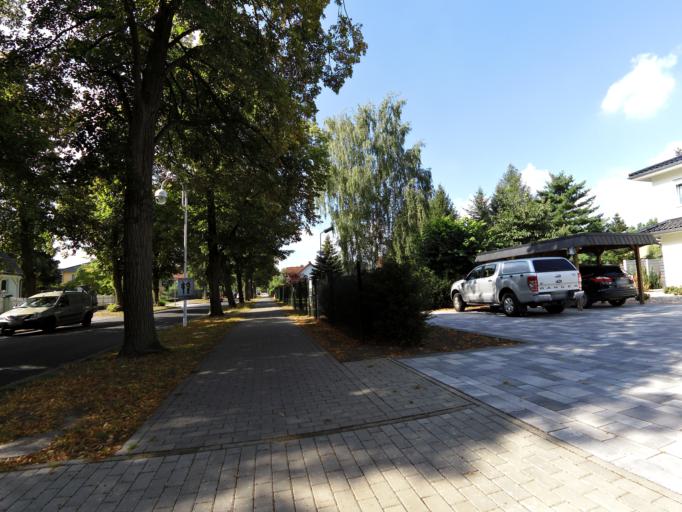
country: DE
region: Berlin
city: Lichtenrade
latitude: 52.3566
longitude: 13.4183
